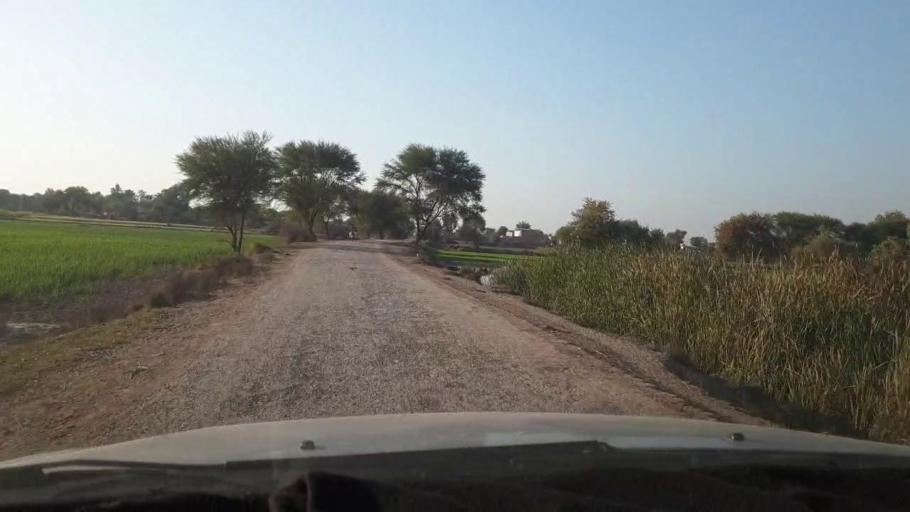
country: PK
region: Sindh
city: Mirpur Mathelo
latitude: 27.9967
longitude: 69.5179
